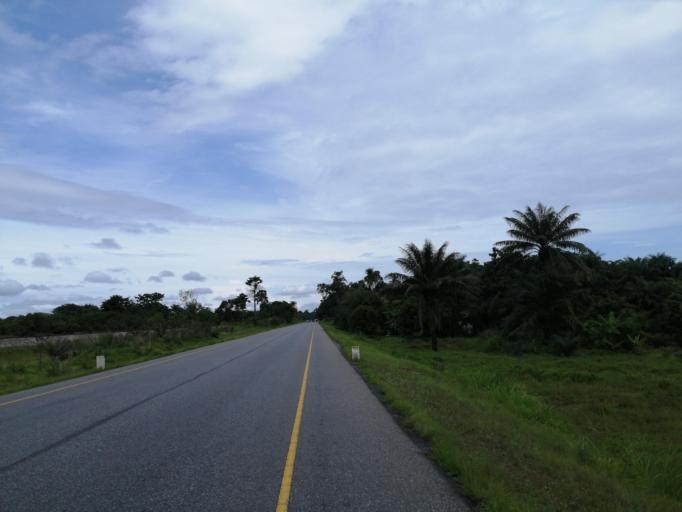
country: SL
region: Northern Province
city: Port Loko
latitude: 8.7448
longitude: -12.9288
